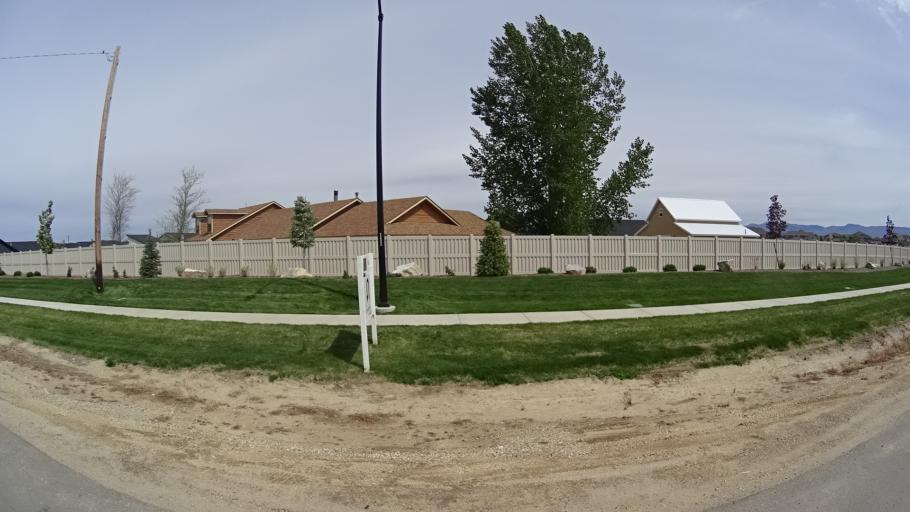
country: US
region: Idaho
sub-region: Ada County
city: Meridian
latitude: 43.5612
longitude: -116.3649
